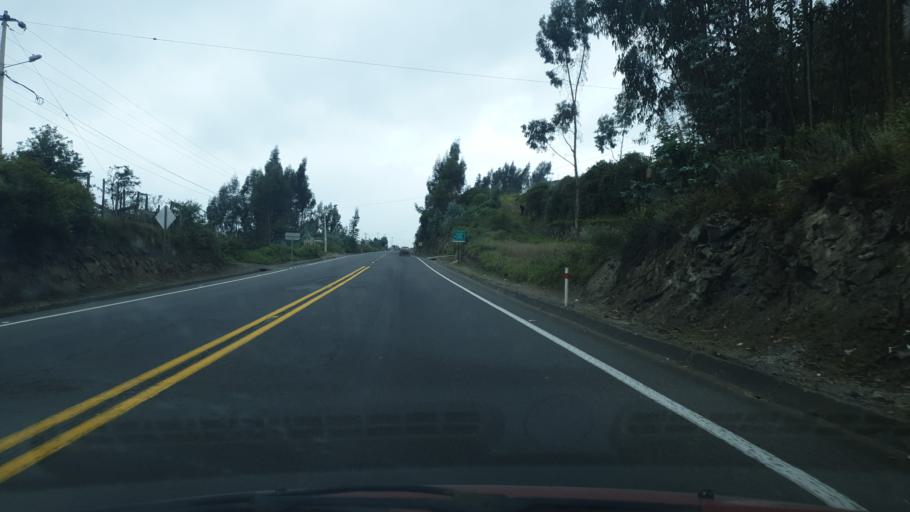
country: EC
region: Tungurahua
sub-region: Canton Quero
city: Quero
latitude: -1.3796
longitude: -78.6494
